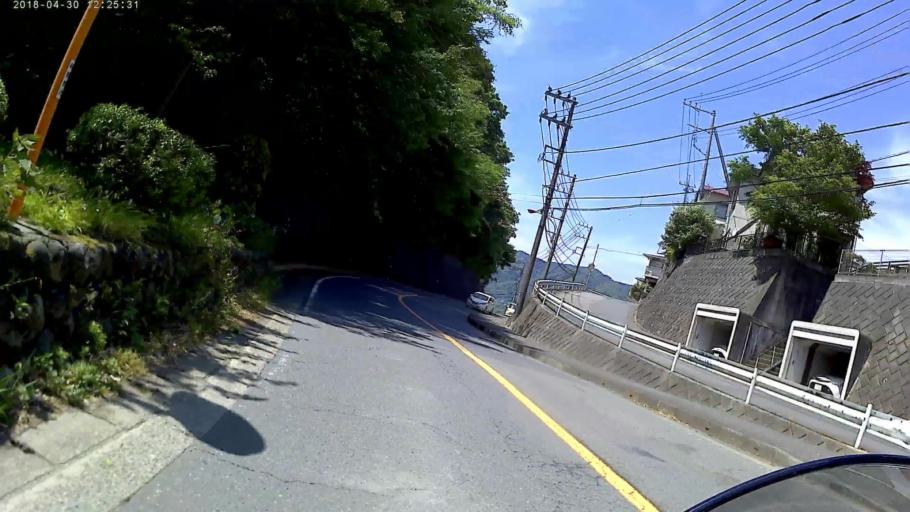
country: JP
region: Tokyo
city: Hachioji
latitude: 35.5806
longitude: 139.2728
